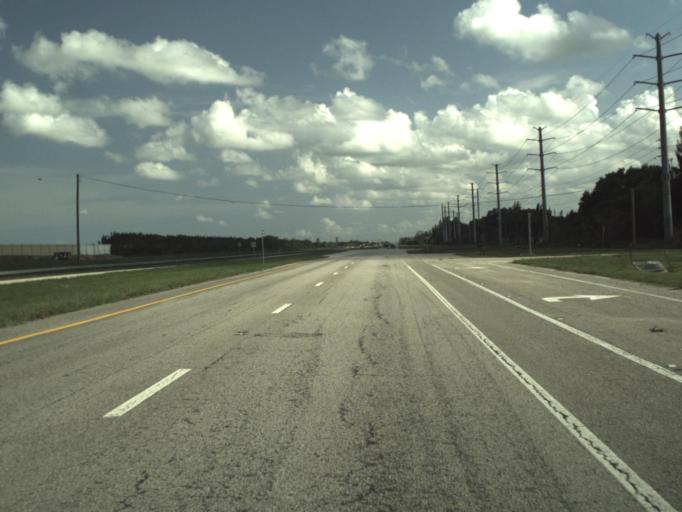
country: US
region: Florida
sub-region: Palm Beach County
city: Villages of Oriole
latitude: 26.4338
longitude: -80.2045
